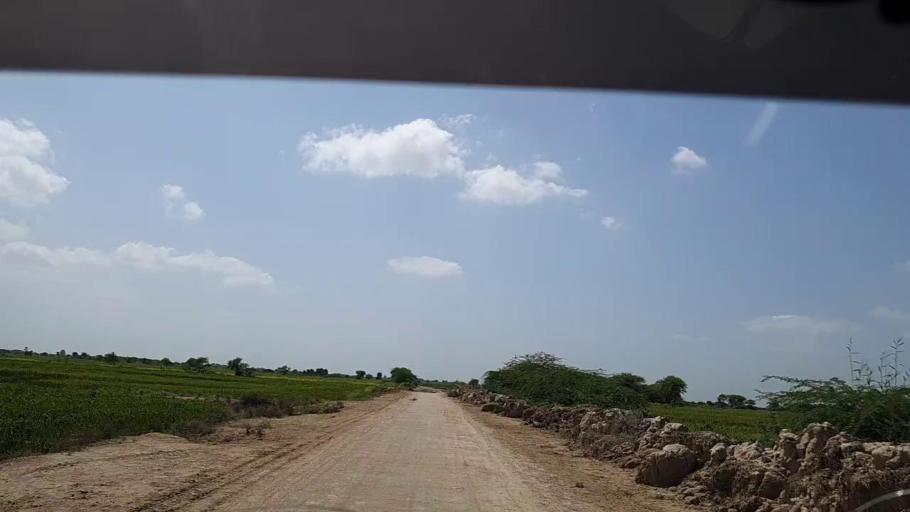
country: PK
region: Sindh
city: Badin
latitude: 24.5604
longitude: 68.7456
